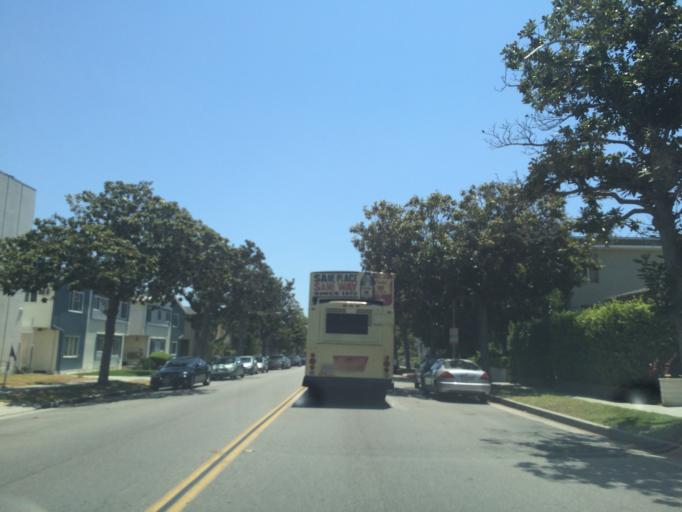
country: US
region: California
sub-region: Los Angeles County
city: Beverly Hills
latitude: 34.0637
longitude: -118.3896
